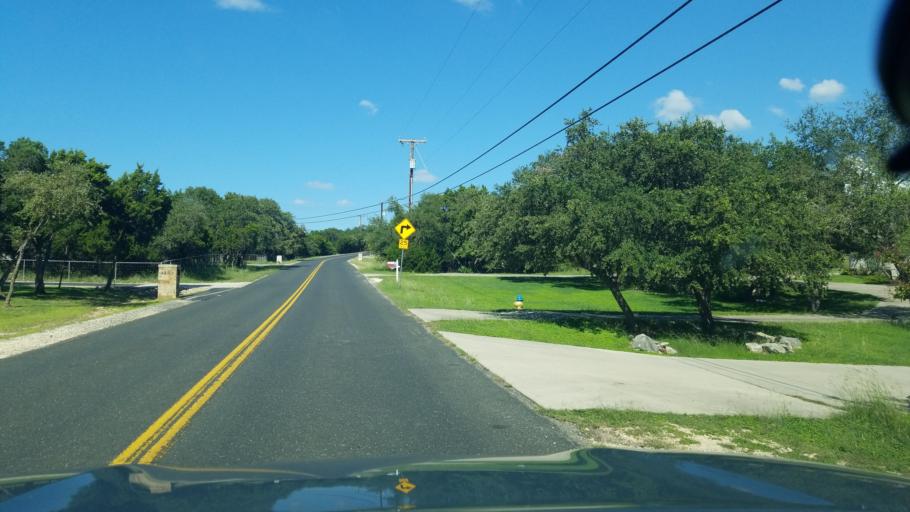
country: US
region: Texas
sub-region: Bexar County
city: Timberwood Park
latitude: 29.6705
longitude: -98.5139
